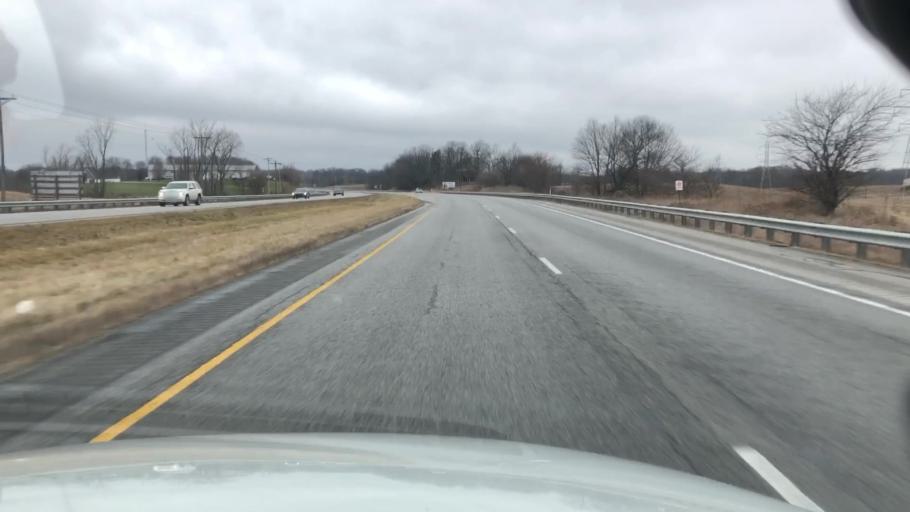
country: US
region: Indiana
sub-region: Whitley County
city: Columbia City
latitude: 41.1725
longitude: -85.5468
